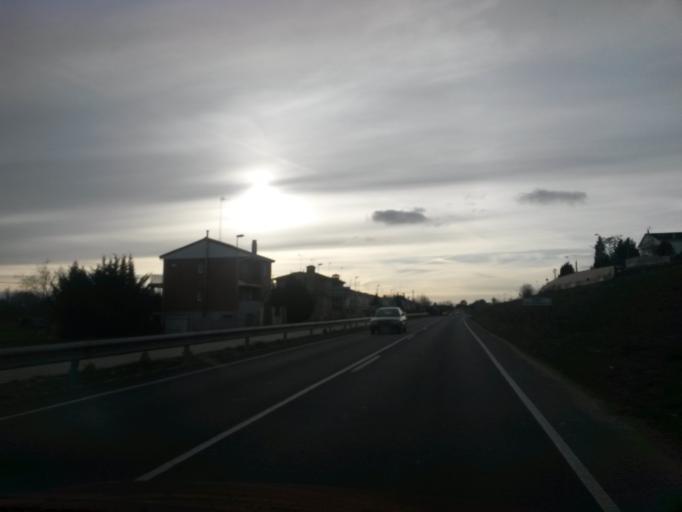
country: ES
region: Castille and Leon
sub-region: Provincia de Salamanca
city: Cabrerizos
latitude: 40.9747
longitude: -5.6126
